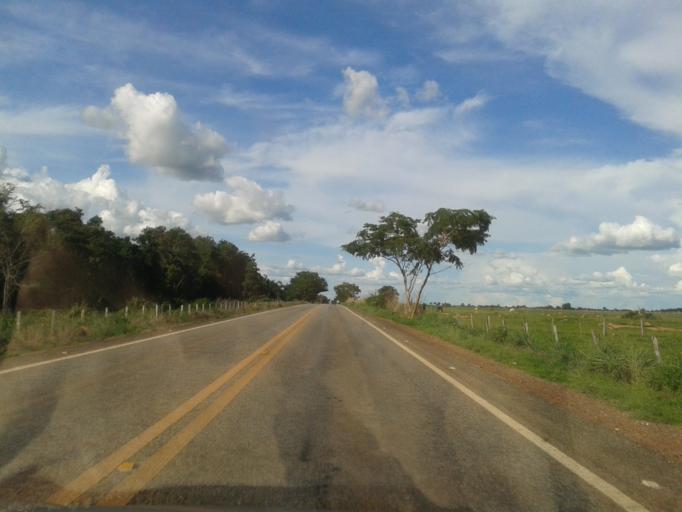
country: BR
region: Goias
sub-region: Mozarlandia
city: Mozarlandia
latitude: -14.5558
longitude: -50.4953
